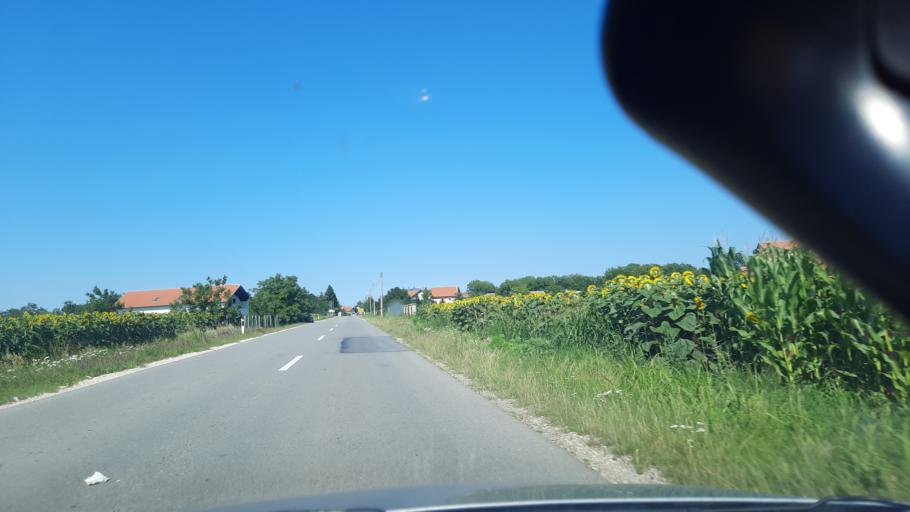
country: RS
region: Central Serbia
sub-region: Branicevski Okrug
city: Malo Crnice
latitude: 44.5809
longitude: 21.3912
